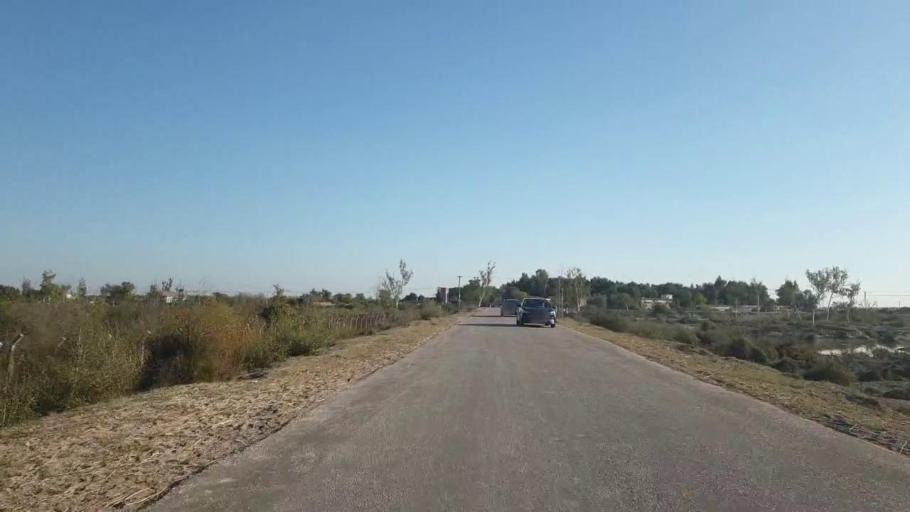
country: PK
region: Sindh
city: Dokri
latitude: 27.3321
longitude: 68.1304
